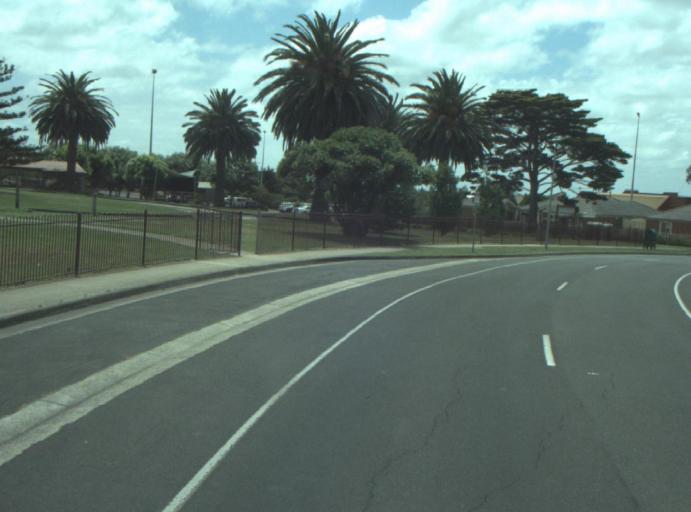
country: AU
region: Victoria
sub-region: Greater Geelong
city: Wandana Heights
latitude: -38.1901
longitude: 144.3236
